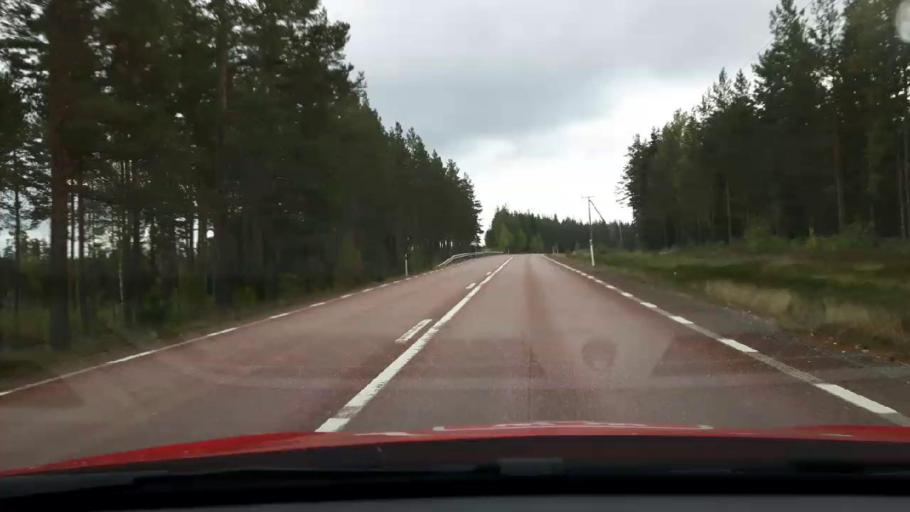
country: SE
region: Gaevleborg
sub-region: Soderhamns Kommun
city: Soderhamn
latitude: 61.1251
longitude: 16.9320
